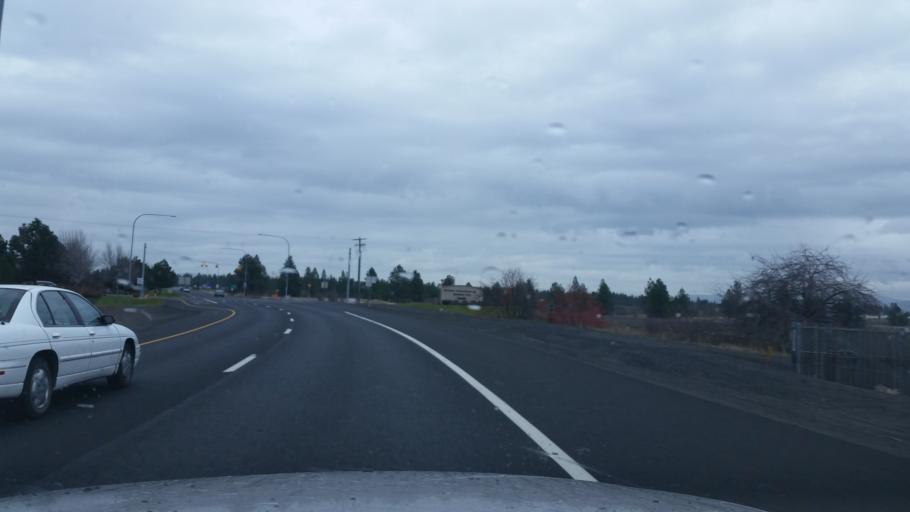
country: US
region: Washington
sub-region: Spokane County
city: Airway Heights
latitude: 47.6347
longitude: -117.5189
